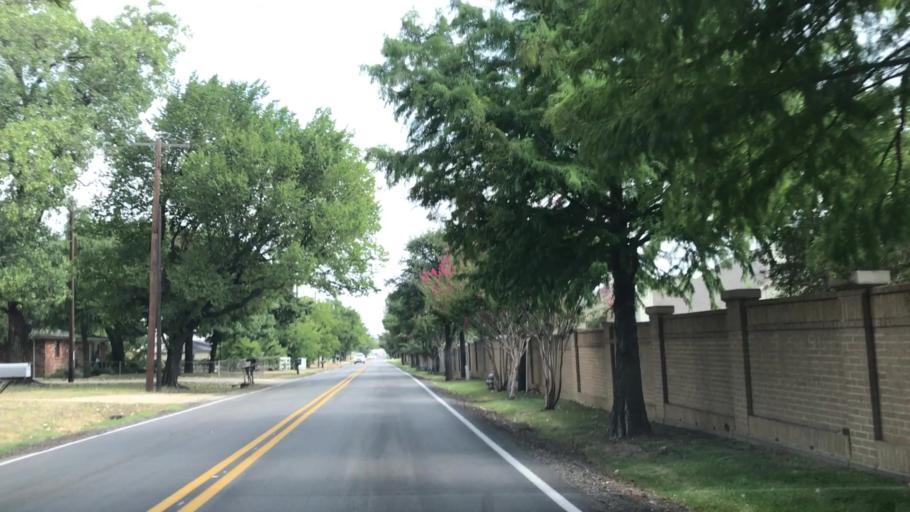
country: US
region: Texas
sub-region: Tarrant County
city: Keller
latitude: 32.9175
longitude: -97.2725
